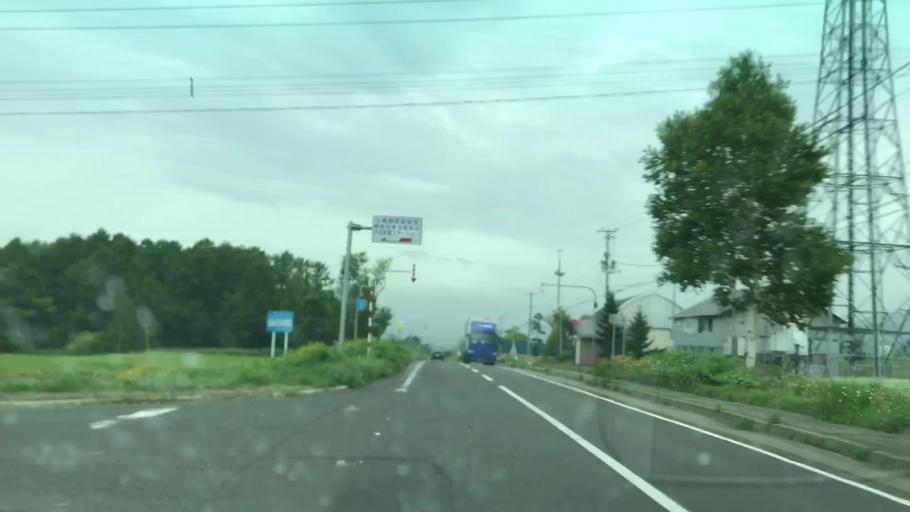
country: JP
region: Hokkaido
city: Niseko Town
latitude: 42.7591
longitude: 140.4770
